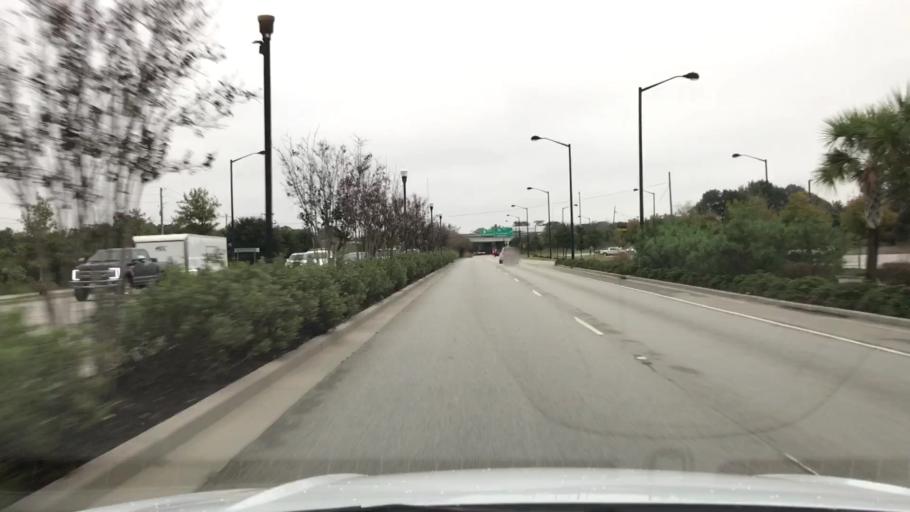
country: US
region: South Carolina
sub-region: Charleston County
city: Mount Pleasant
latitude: 32.8134
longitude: -79.8532
